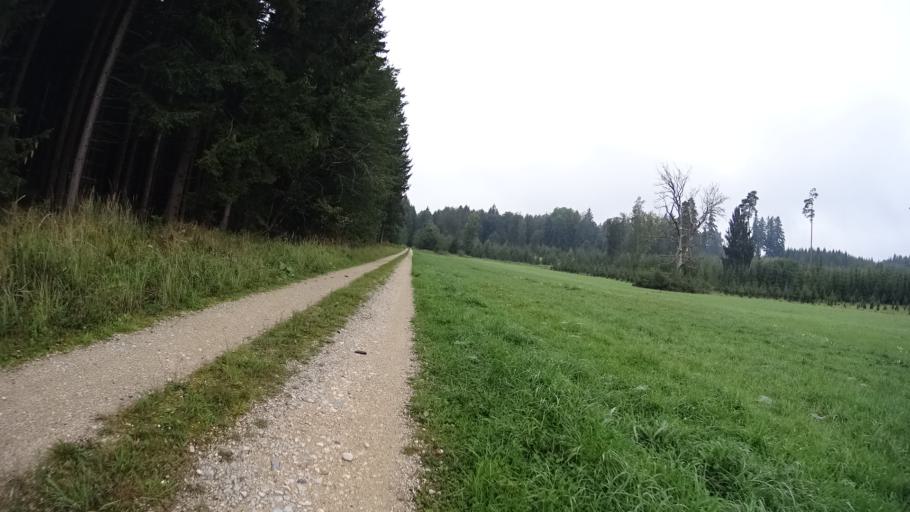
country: DE
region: Bavaria
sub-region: Upper Bavaria
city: Denkendorf
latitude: 48.8963
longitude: 11.4624
